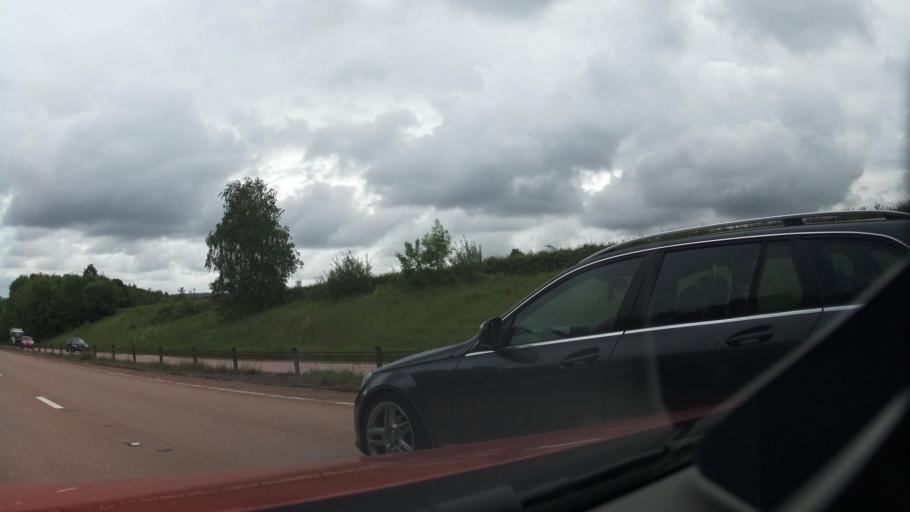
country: GB
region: England
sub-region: Devon
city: Ottery St Mary
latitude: 50.7670
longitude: -3.3076
